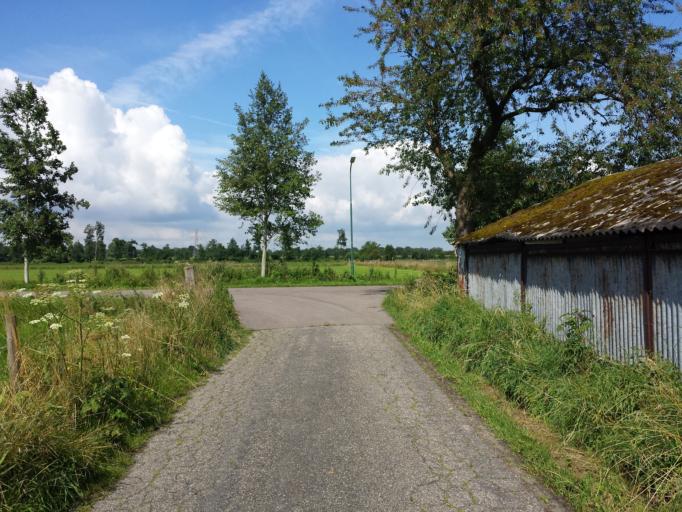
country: NL
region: Utrecht
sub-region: Gemeente Utrechtse Heuvelrug
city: Overberg
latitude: 52.0420
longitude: 5.5047
